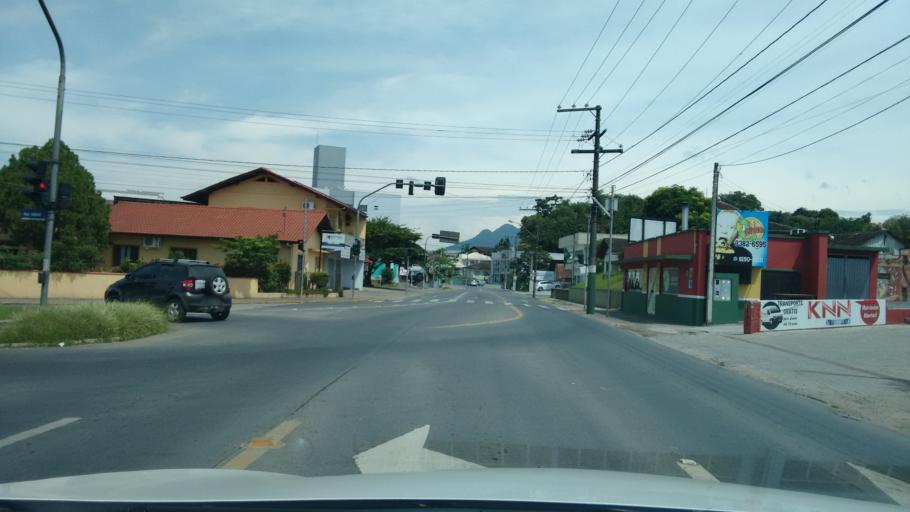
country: BR
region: Santa Catarina
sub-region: Timbo
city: Timbo
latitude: -26.8379
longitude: -49.2733
